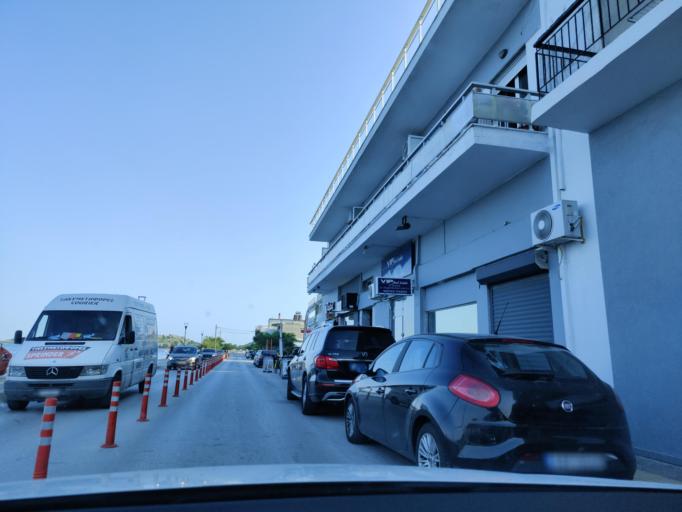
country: GR
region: East Macedonia and Thrace
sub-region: Nomos Kavalas
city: Nea Peramos
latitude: 40.8372
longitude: 24.3052
